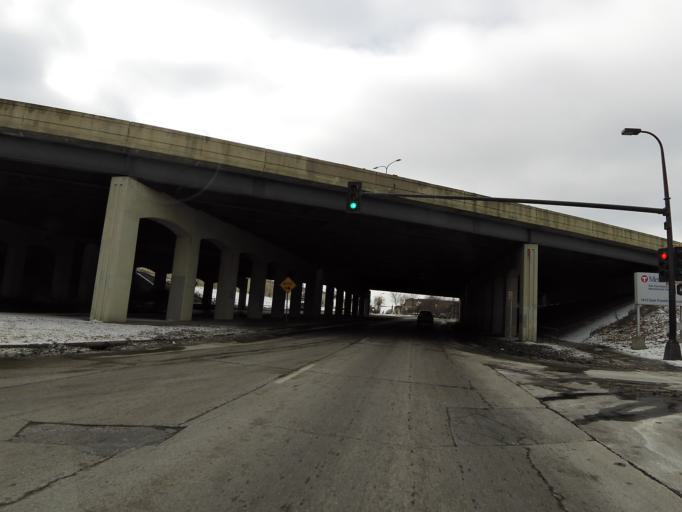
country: US
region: Minnesota
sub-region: Hennepin County
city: Minneapolis
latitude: 44.9627
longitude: -93.2487
